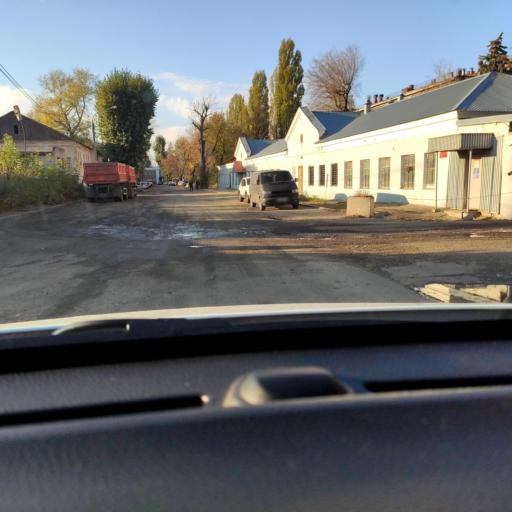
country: RU
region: Voronezj
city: Voronezh
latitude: 51.6759
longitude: 39.1748
